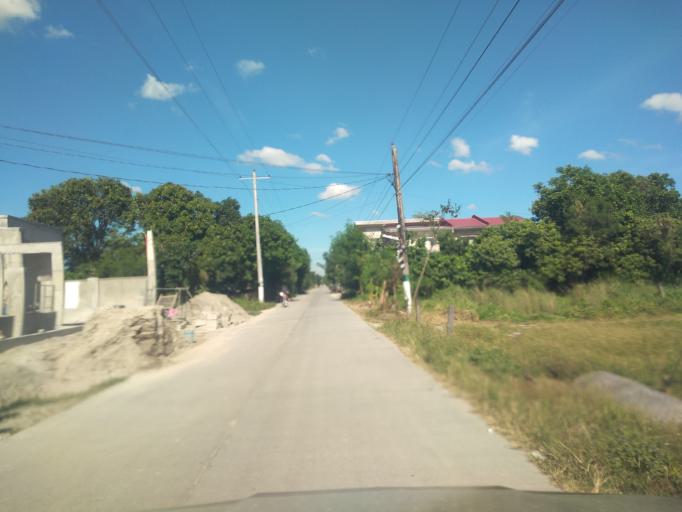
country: PH
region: Central Luzon
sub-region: Province of Pampanga
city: Bacolor
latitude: 15.0082
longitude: 120.6391
